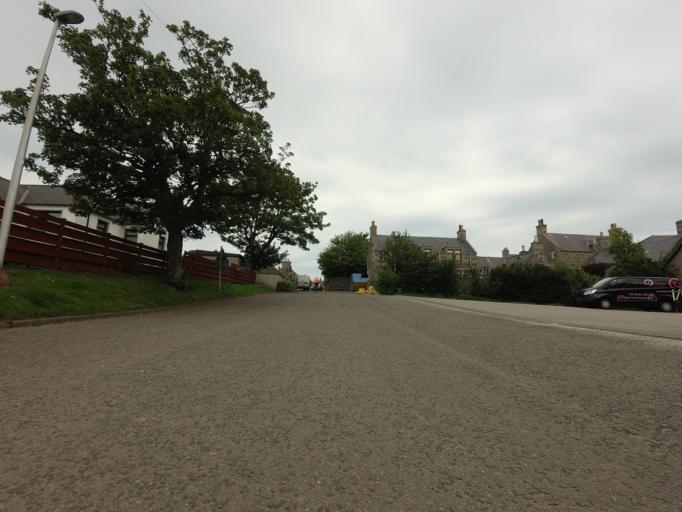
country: GB
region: Scotland
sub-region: Aberdeenshire
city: Portsoy
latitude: 57.6805
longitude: -2.6900
